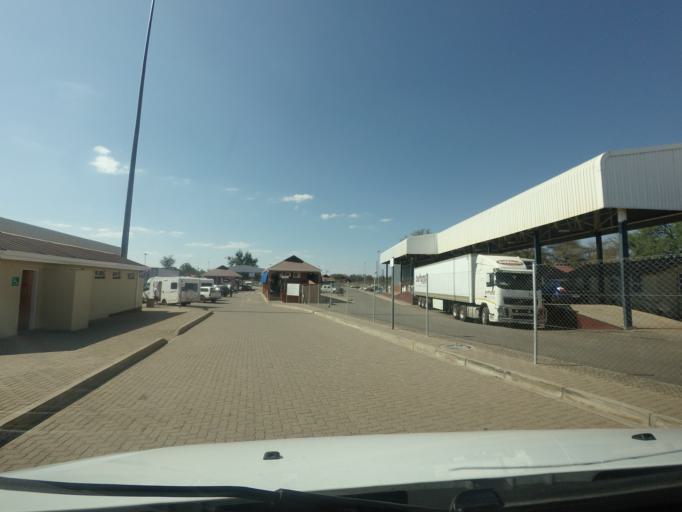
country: BW
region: Central
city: Makobeng
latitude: -22.9997
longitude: 27.9440
